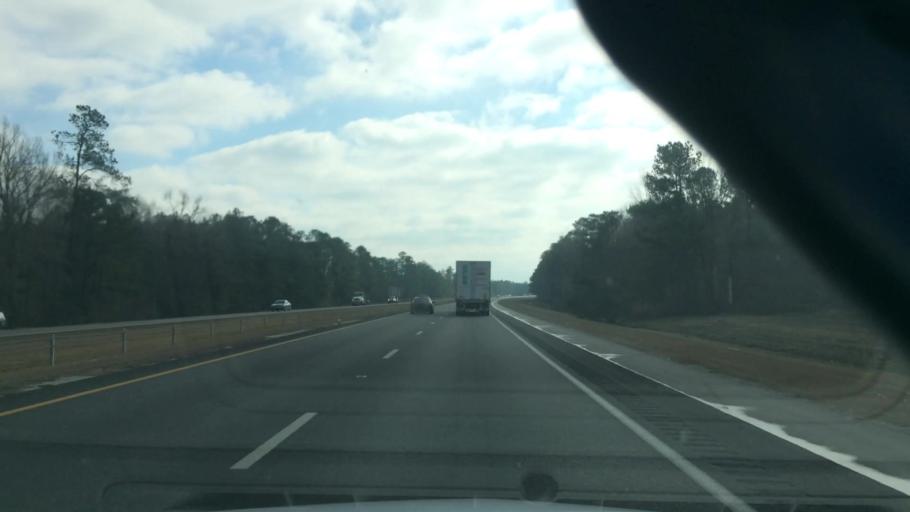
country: US
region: North Carolina
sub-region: Pender County
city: Burgaw
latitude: 34.5600
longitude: -77.8957
